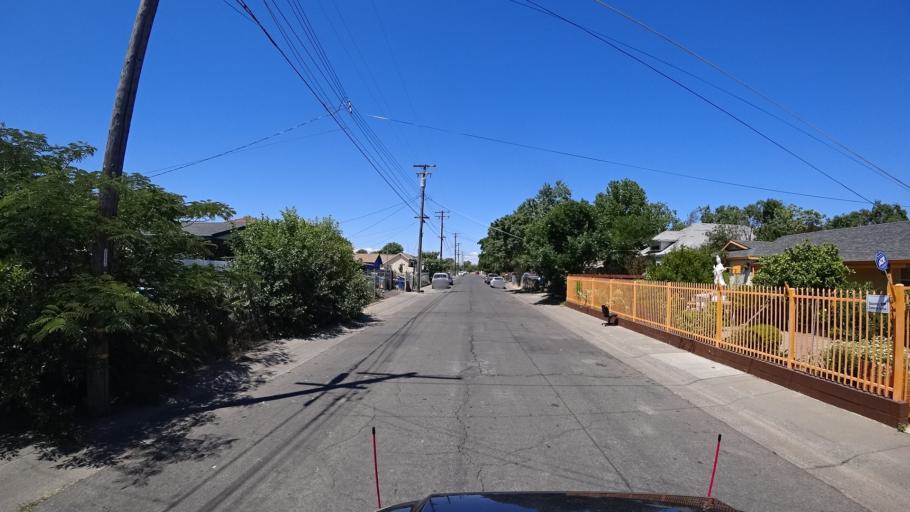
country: US
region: California
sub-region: Sacramento County
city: Florin
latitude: 38.5189
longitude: -121.4158
